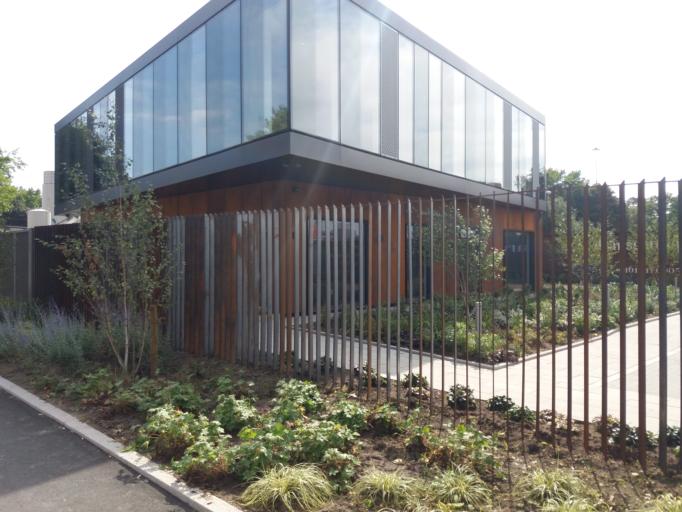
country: GB
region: England
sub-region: Manchester
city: Hulme
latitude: 53.4721
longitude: -2.2537
